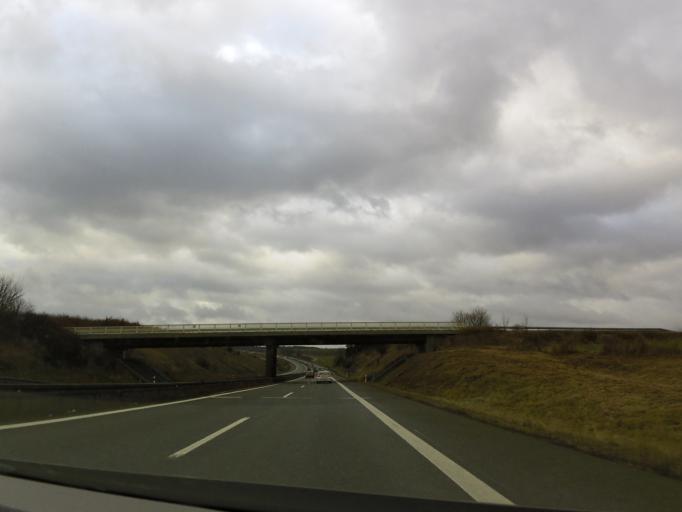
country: DE
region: Bavaria
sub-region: Upper Franconia
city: Regnitzlosau
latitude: 50.2945
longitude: 12.0256
